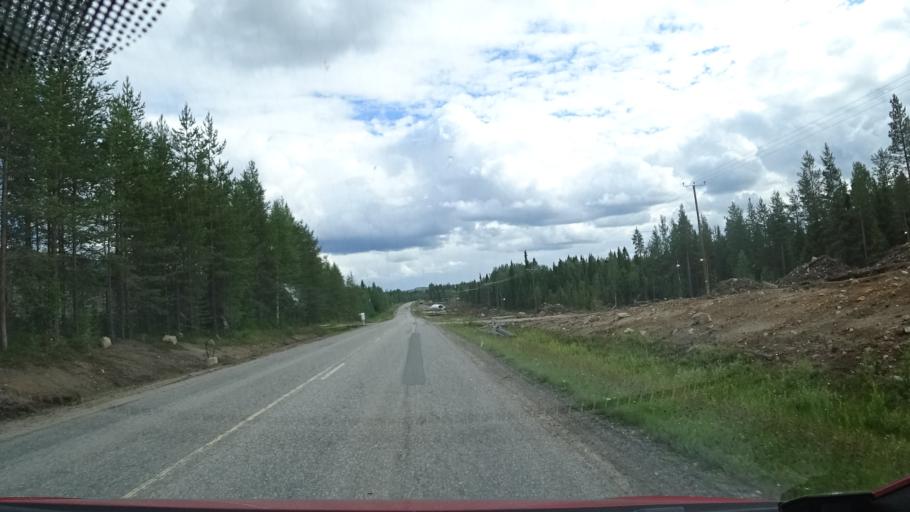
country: FI
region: Lapland
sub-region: Rovaniemi
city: Rovaniemi
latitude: 66.5405
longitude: 25.7176
